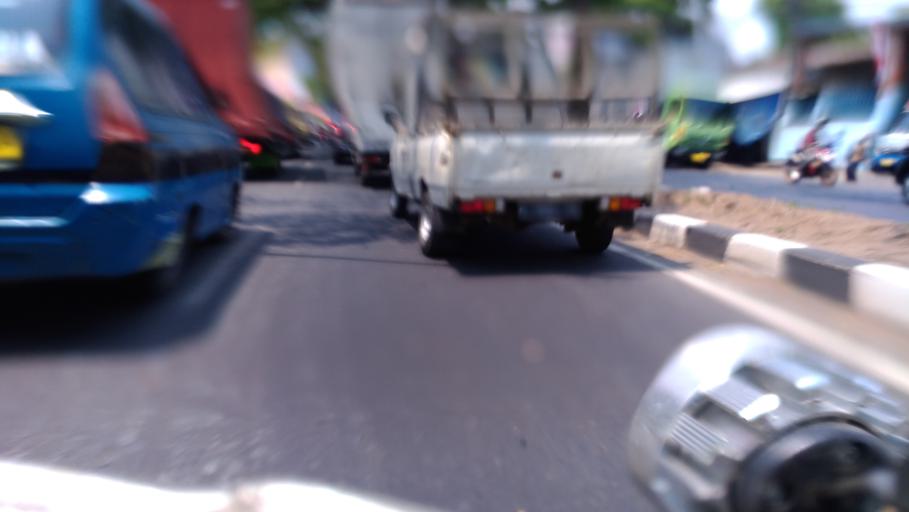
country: ID
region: West Java
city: Cileungsir
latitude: -6.3872
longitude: 106.9398
